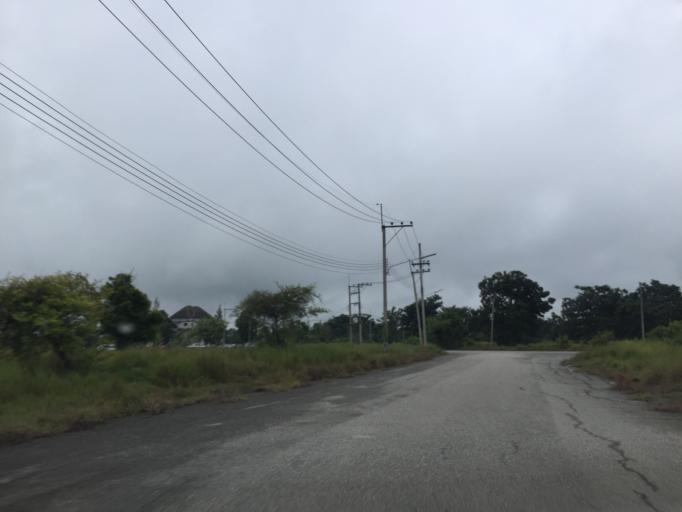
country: TH
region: Lamphun
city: Ban Thi
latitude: 18.6724
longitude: 99.1044
